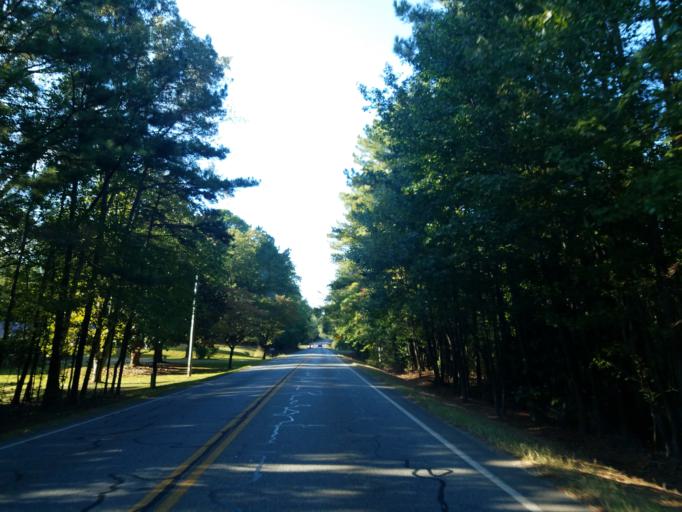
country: US
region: Georgia
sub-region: Bartow County
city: Cartersville
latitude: 34.0944
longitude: -84.8450
